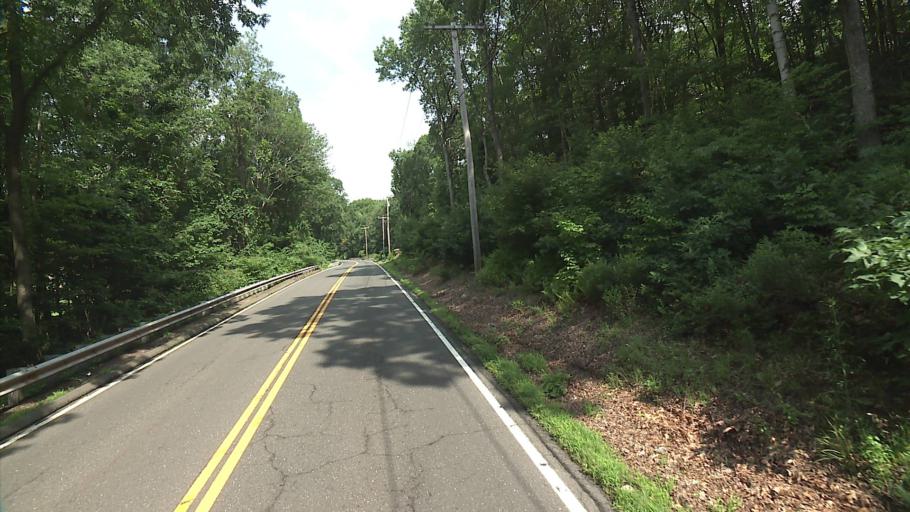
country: US
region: Connecticut
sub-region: New Haven County
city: Wolcott
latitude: 41.6008
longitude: -72.9680
